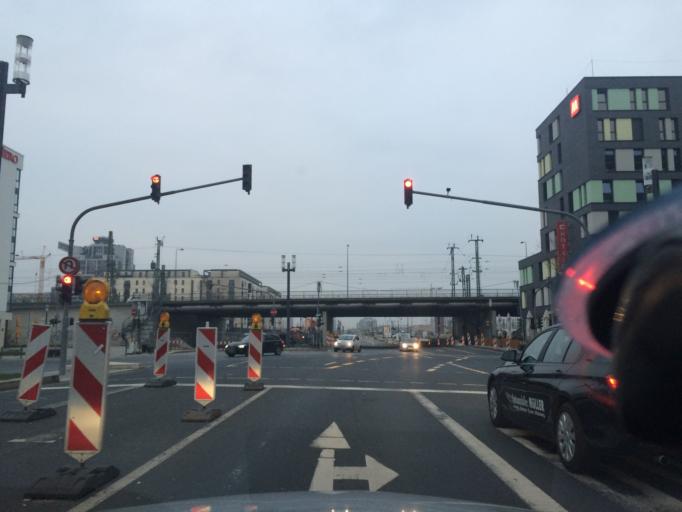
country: DE
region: Hesse
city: Niederrad
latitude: 50.1086
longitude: 8.6448
